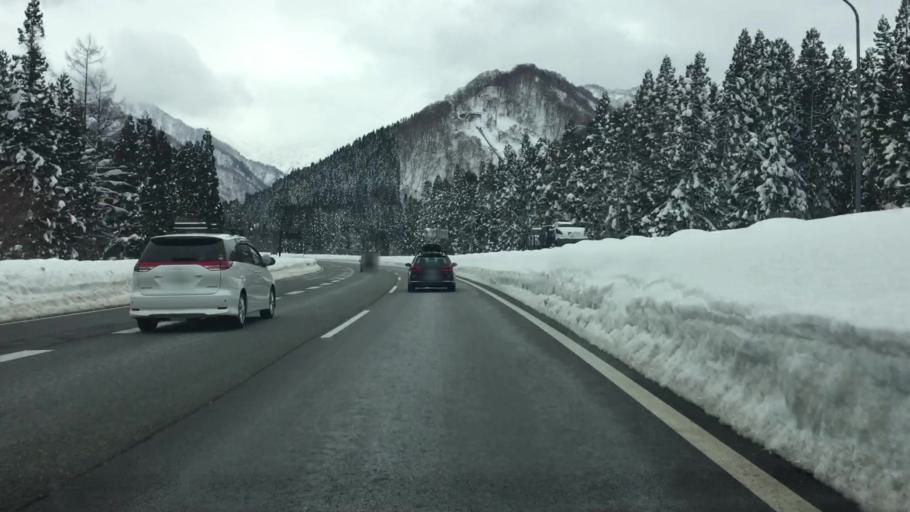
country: JP
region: Niigata
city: Shiozawa
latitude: 36.8828
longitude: 138.8527
